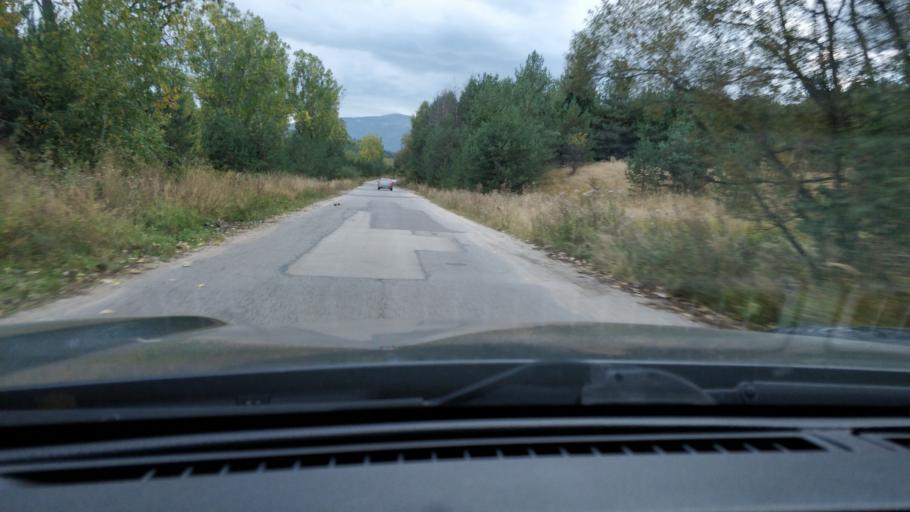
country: BG
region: Sofiya
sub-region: Obshtina Samokov
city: Samokov
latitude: 42.4806
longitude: 23.3960
